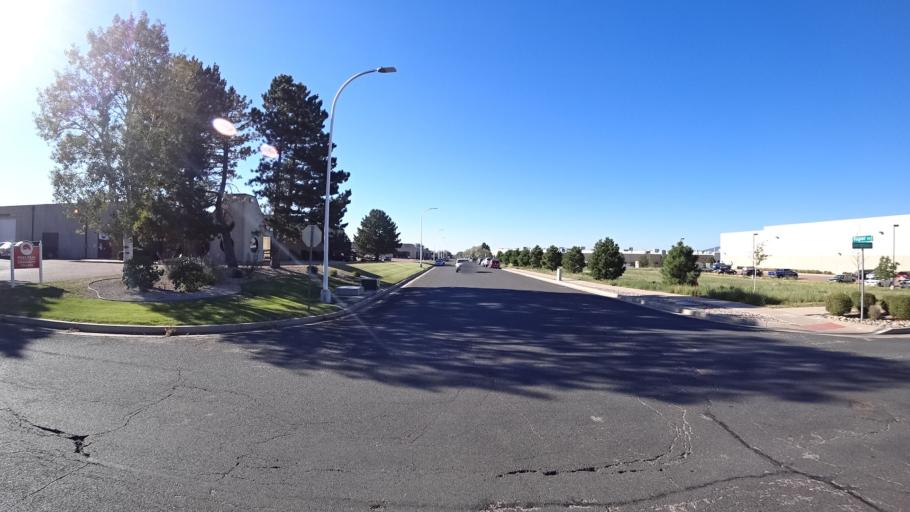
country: US
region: Colorado
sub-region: El Paso County
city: Cimarron Hills
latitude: 38.8143
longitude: -104.7253
